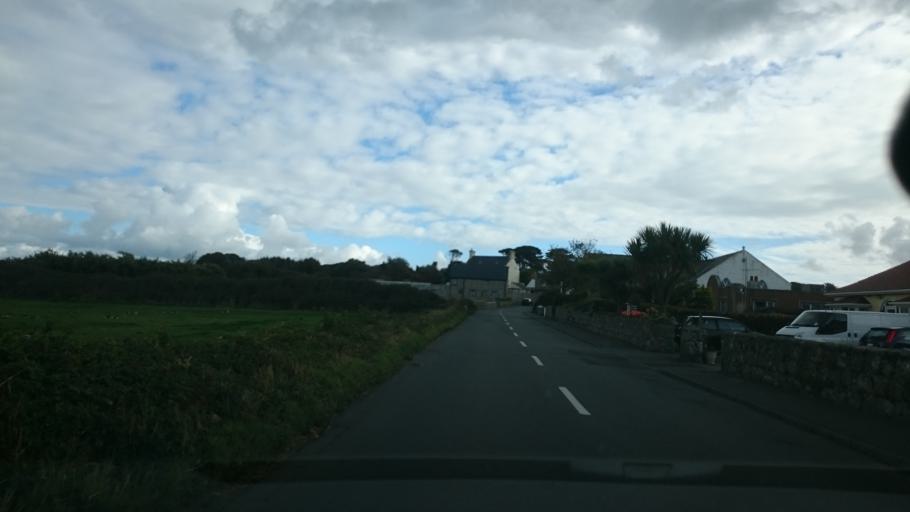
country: GG
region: St Peter Port
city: Saint Peter Port
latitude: 49.4538
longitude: -2.6484
